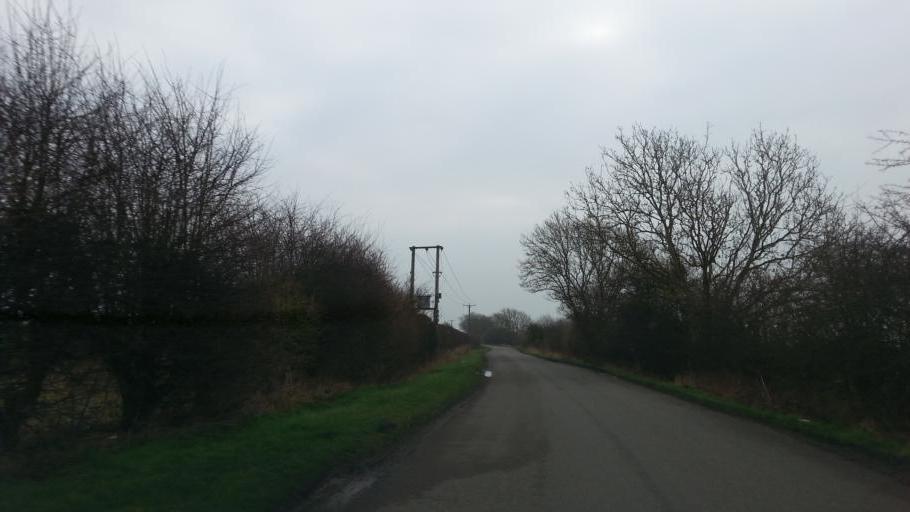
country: GB
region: England
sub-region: Lincolnshire
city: Long Bennington
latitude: 53.0057
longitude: -0.7992
